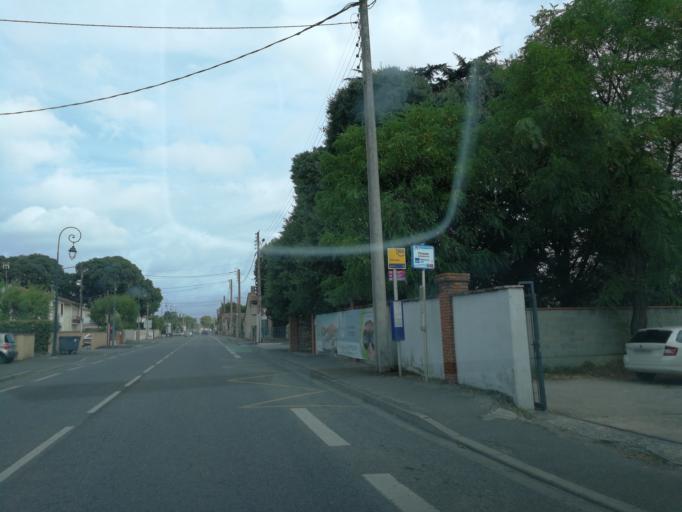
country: FR
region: Midi-Pyrenees
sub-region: Departement de la Haute-Garonne
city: Aucamville
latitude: 43.6715
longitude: 1.4271
